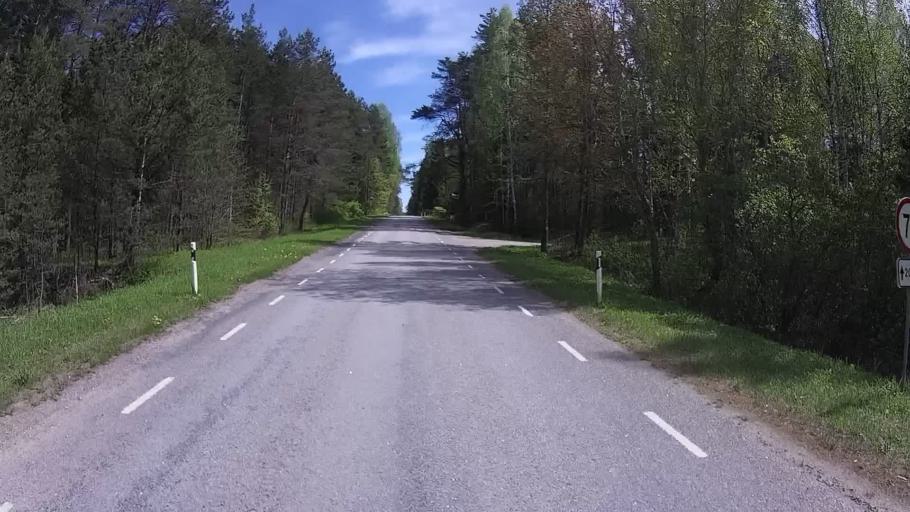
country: LV
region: Apes Novads
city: Ape
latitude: 57.6103
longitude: 26.4435
